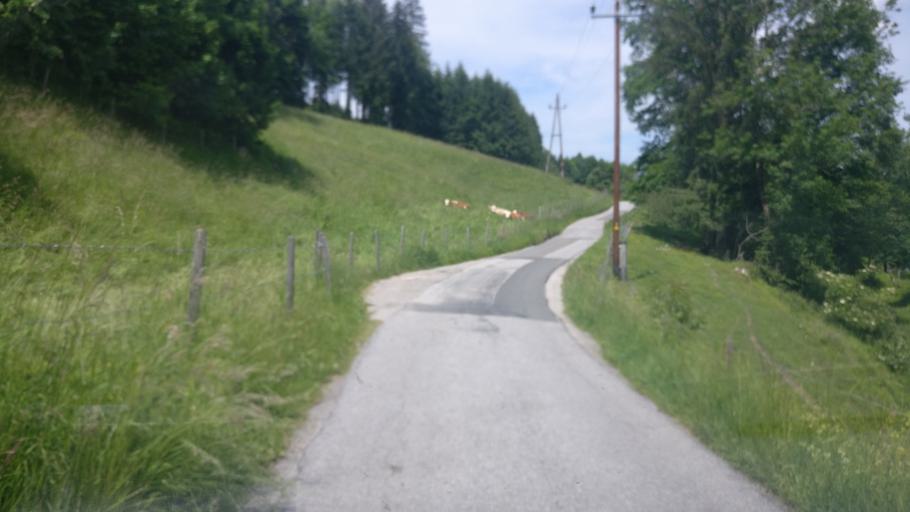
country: AT
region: Salzburg
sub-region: Politischer Bezirk Hallein
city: Kuchl
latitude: 47.6482
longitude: 13.1209
